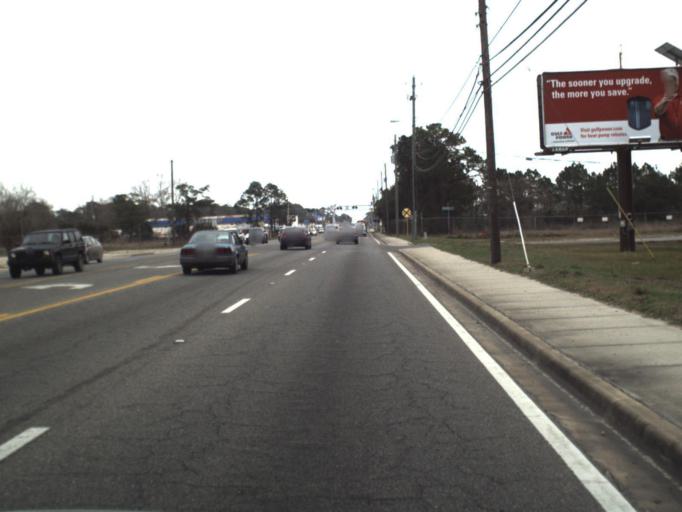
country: US
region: Florida
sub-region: Bay County
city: Cedar Grove
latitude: 30.1749
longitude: -85.6382
